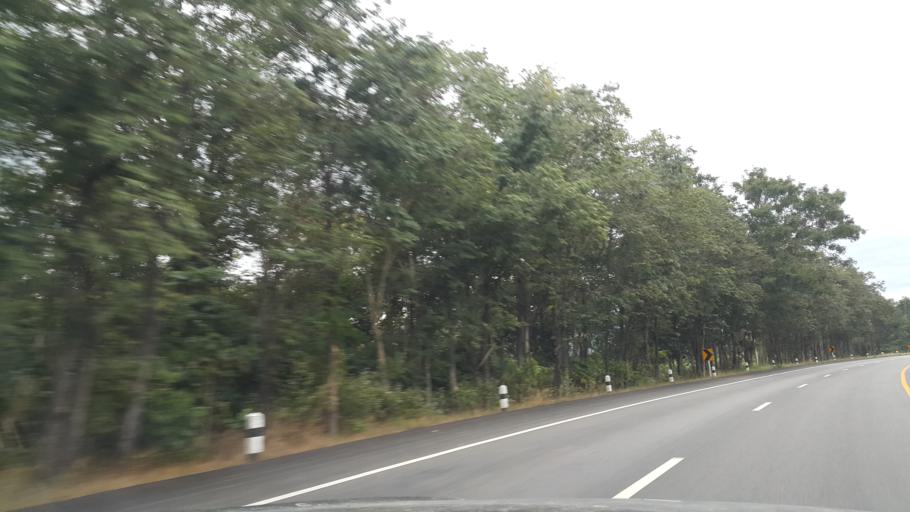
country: TH
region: Lampang
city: Thoen
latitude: 17.7399
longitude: 99.2331
